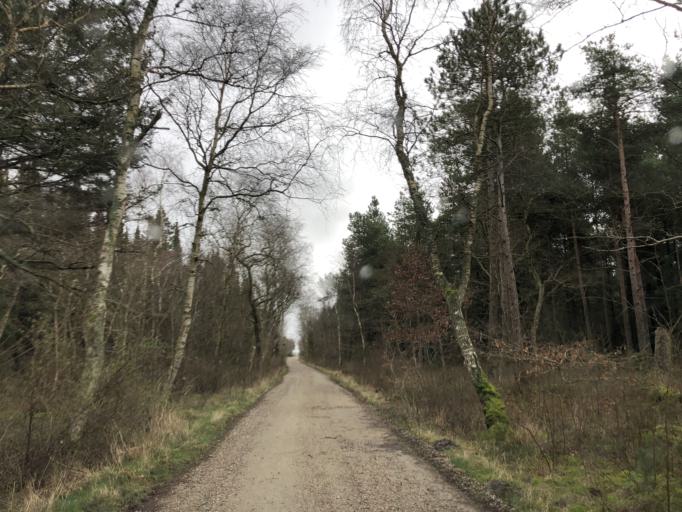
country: DK
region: Central Jutland
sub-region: Holstebro Kommune
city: Ulfborg
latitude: 56.2954
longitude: 8.1802
